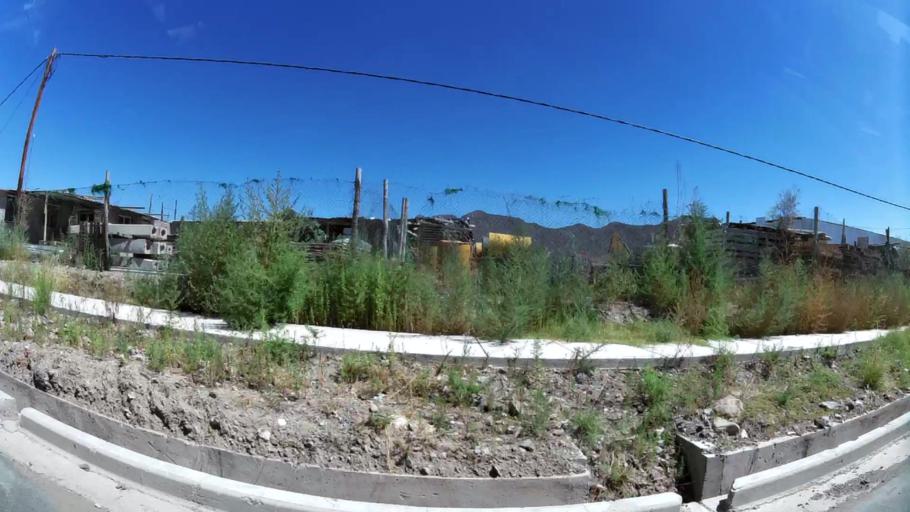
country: AR
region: Mendoza
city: Las Heras
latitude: -32.8353
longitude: -68.8703
